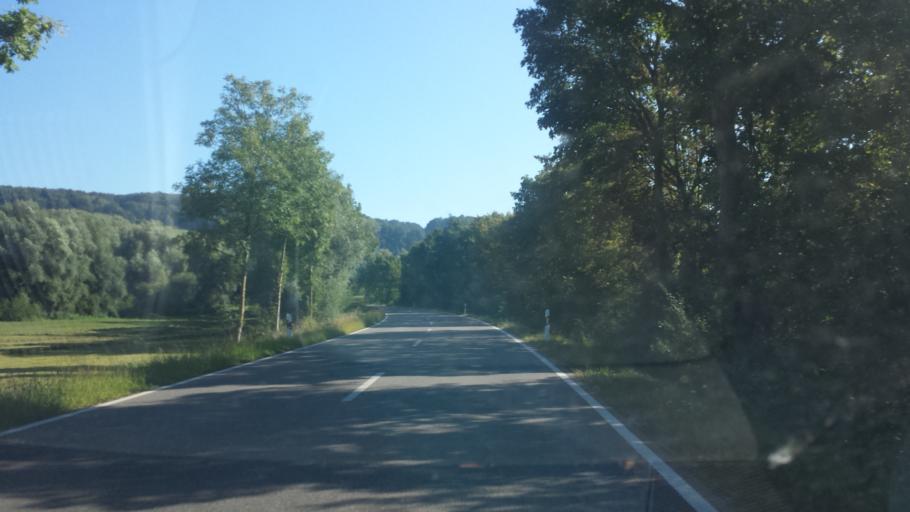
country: DE
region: Bavaria
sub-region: Lower Bavaria
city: Essing
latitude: 48.8871
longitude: 11.8215
